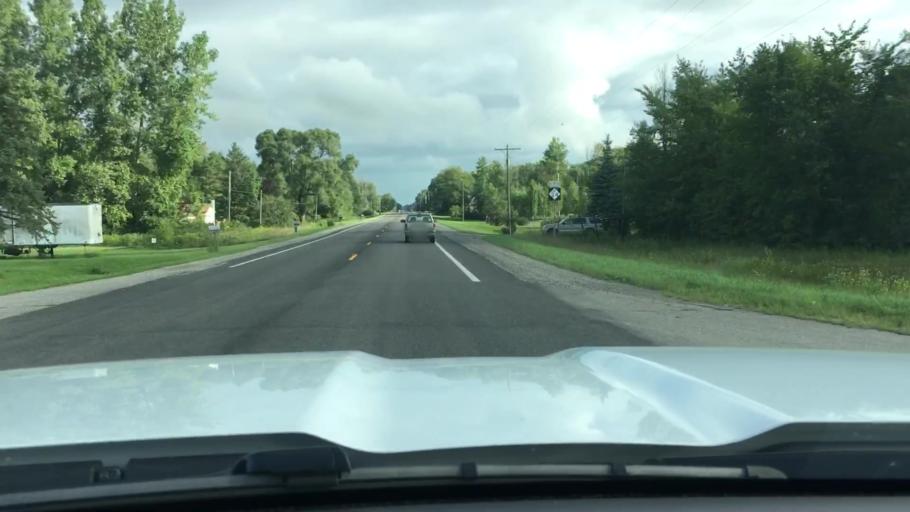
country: US
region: Michigan
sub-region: Tuscola County
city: Caro
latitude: 43.4386
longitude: -83.3851
